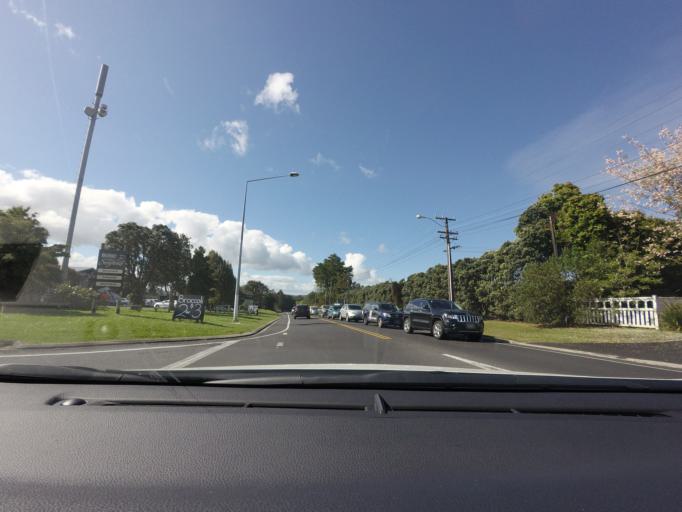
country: NZ
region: Auckland
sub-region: Auckland
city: Rosebank
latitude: -36.7879
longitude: 174.5837
